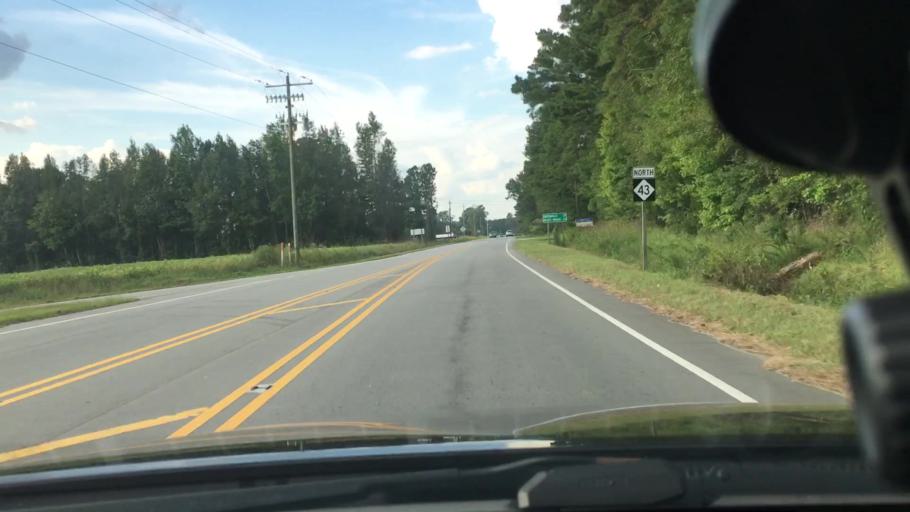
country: US
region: North Carolina
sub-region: Craven County
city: Vanceboro
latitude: 35.3130
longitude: -77.1615
